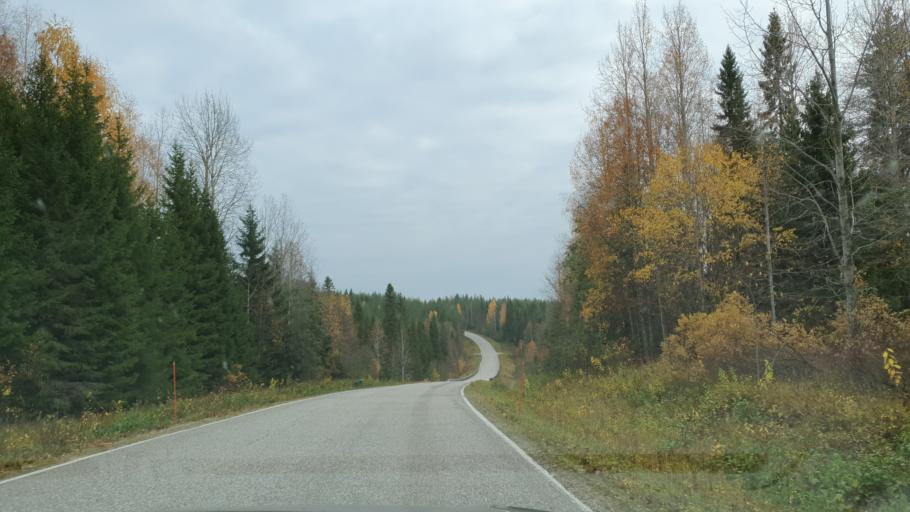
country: FI
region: Kainuu
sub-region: Kajaani
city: Ristijaervi
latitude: 64.4743
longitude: 28.2870
